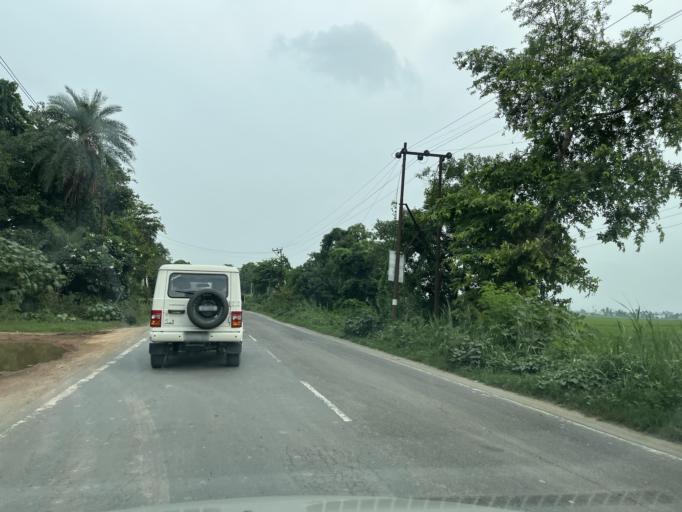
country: IN
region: Uttar Pradesh
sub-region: Rampur
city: Bilaspur
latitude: 29.0262
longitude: 79.2693
